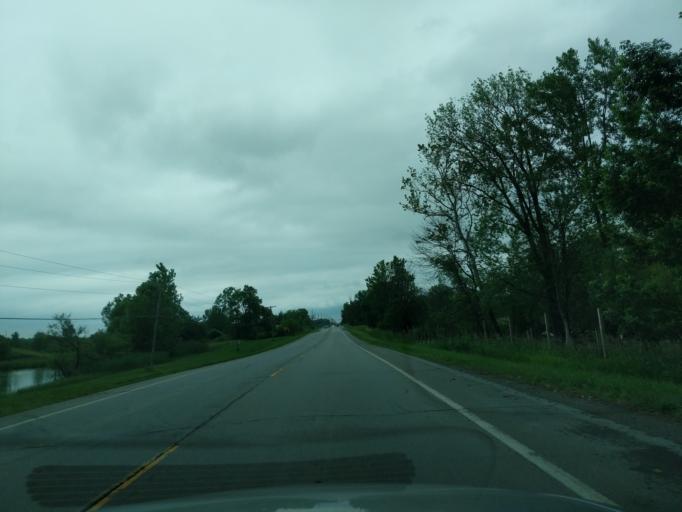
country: US
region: Indiana
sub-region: Hamilton County
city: Noblesville
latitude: 40.0832
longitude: -86.0143
